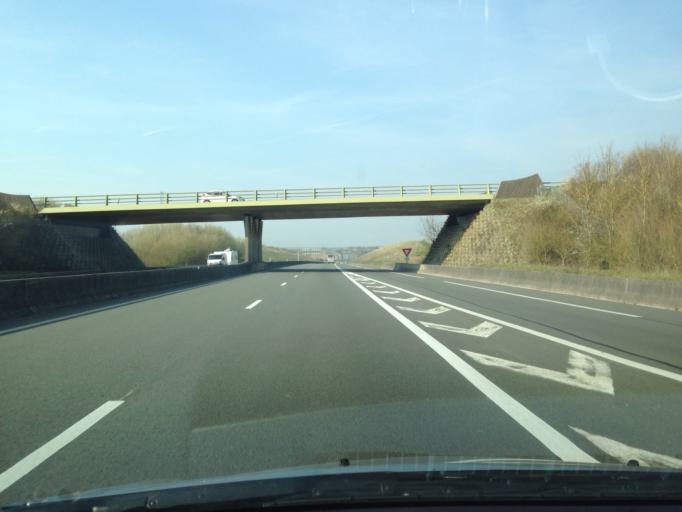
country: FR
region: Nord-Pas-de-Calais
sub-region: Departement du Pas-de-Calais
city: Verton
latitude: 50.4083
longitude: 1.6936
